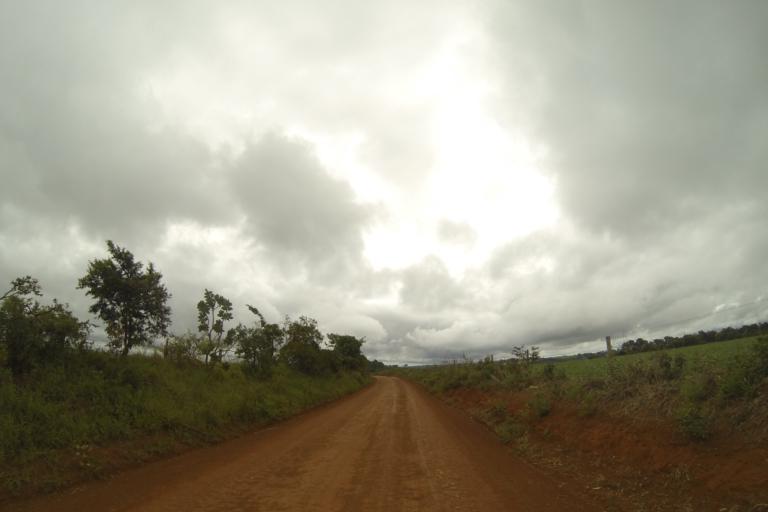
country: BR
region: Minas Gerais
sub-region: Campos Altos
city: Campos Altos
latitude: -19.8586
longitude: -46.3113
